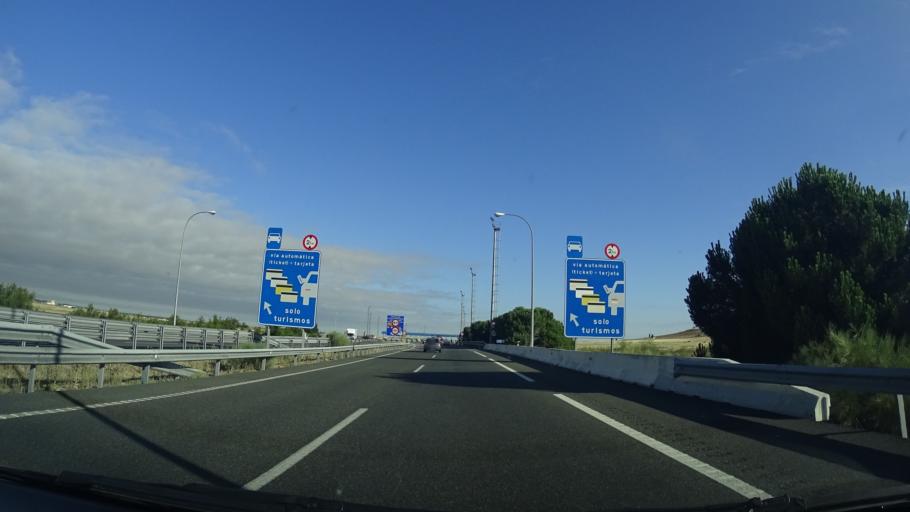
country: ES
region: Castille and Leon
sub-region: Provincia de Avila
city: Sanchidrian
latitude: 40.8799
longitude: -4.5690
